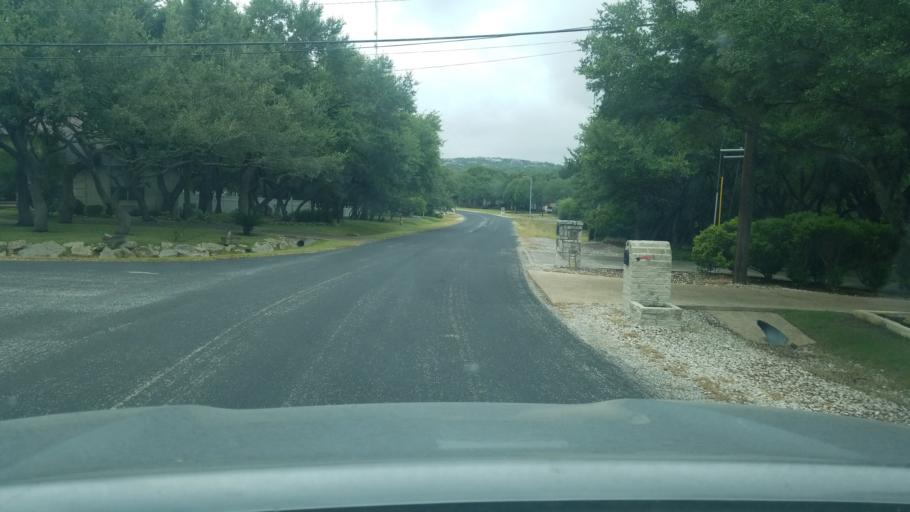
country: US
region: Texas
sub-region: Bexar County
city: Timberwood Park
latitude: 29.7022
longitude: -98.5095
